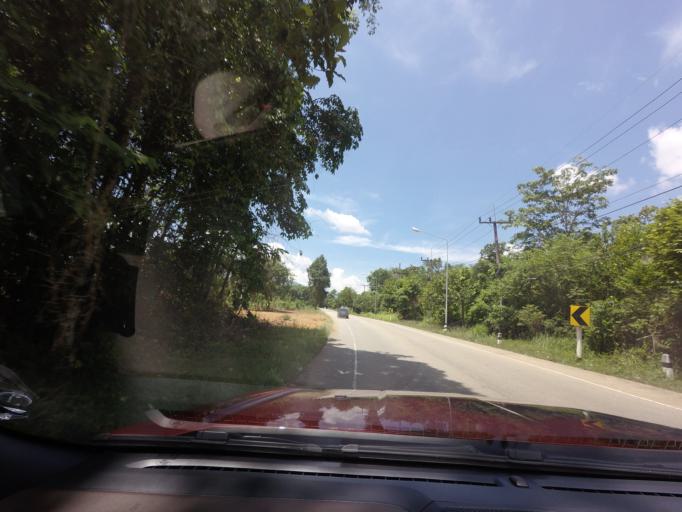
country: TH
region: Narathiwat
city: Chanae
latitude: 6.1878
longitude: 101.6922
